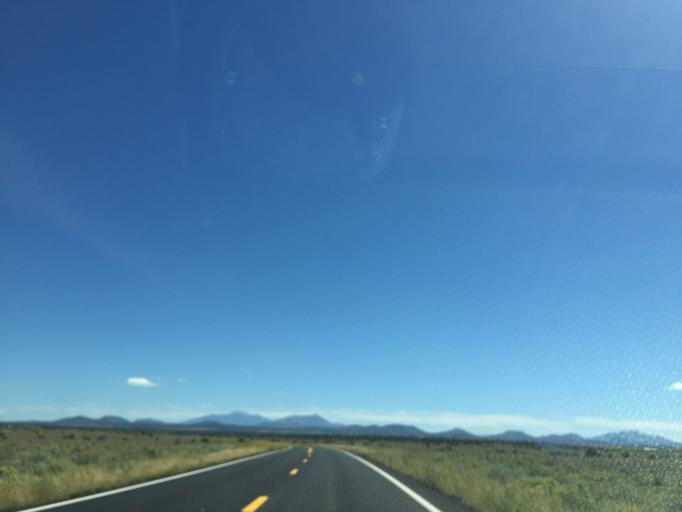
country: US
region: Arizona
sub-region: Coconino County
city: Williams
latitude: 35.6259
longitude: -112.1131
